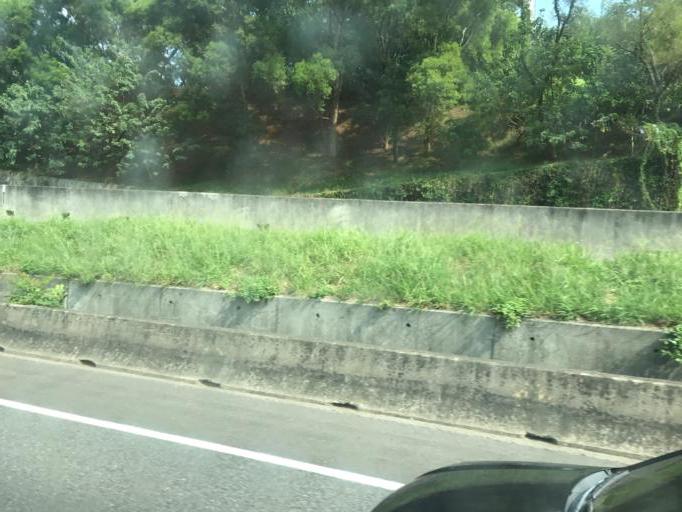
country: TW
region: Taiwan
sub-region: Hsinchu
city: Hsinchu
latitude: 24.7723
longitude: 121.0035
